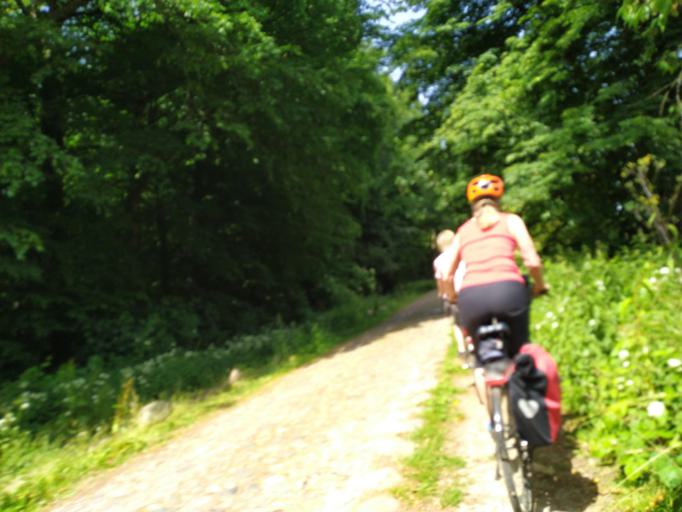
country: DE
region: Schleswig-Holstein
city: Fredeburg
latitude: 53.6673
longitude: 10.7264
